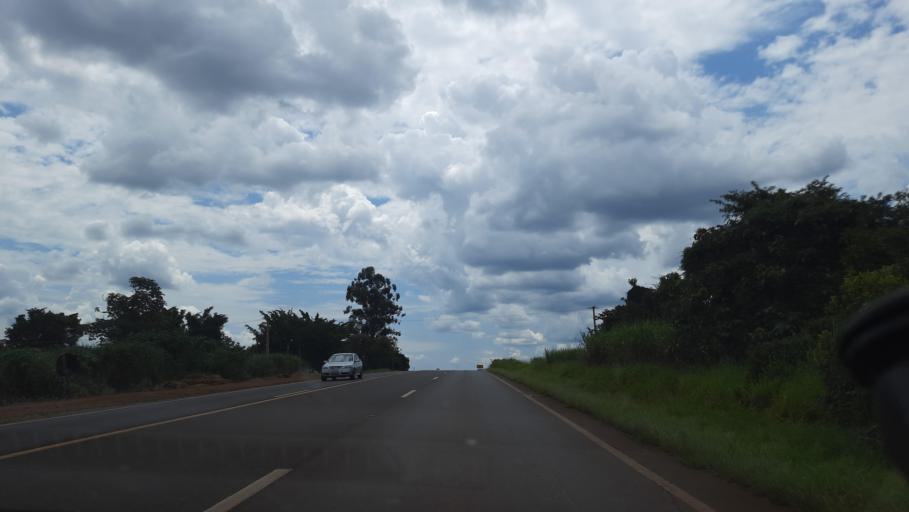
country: BR
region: Sao Paulo
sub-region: Cajuru
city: Cajuru
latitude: -21.2891
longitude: -47.2840
